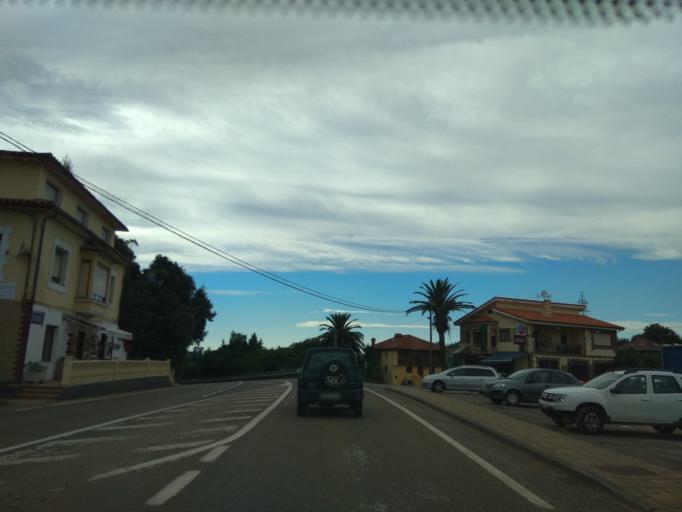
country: ES
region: Cantabria
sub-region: Provincia de Cantabria
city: Entrambasaguas
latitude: 43.3897
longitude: -3.7178
